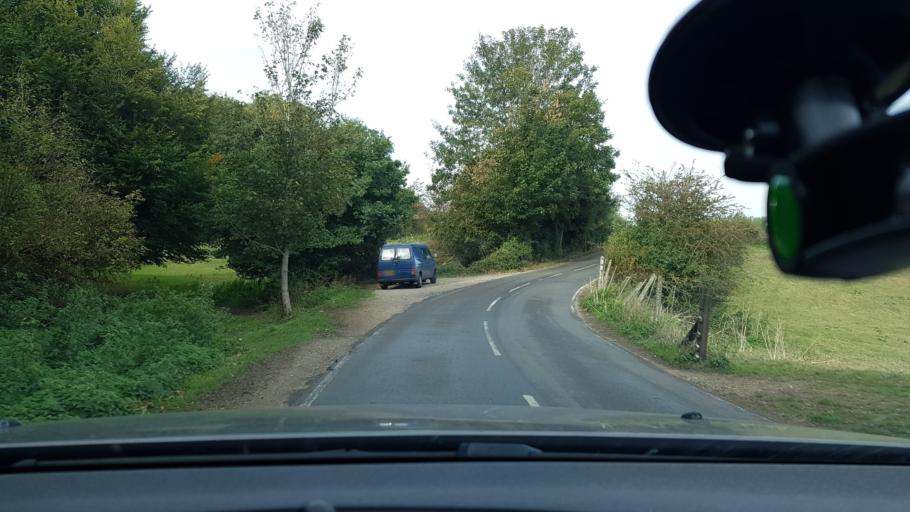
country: GB
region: England
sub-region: West Berkshire
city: Hungerford
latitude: 51.4104
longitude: -1.4958
